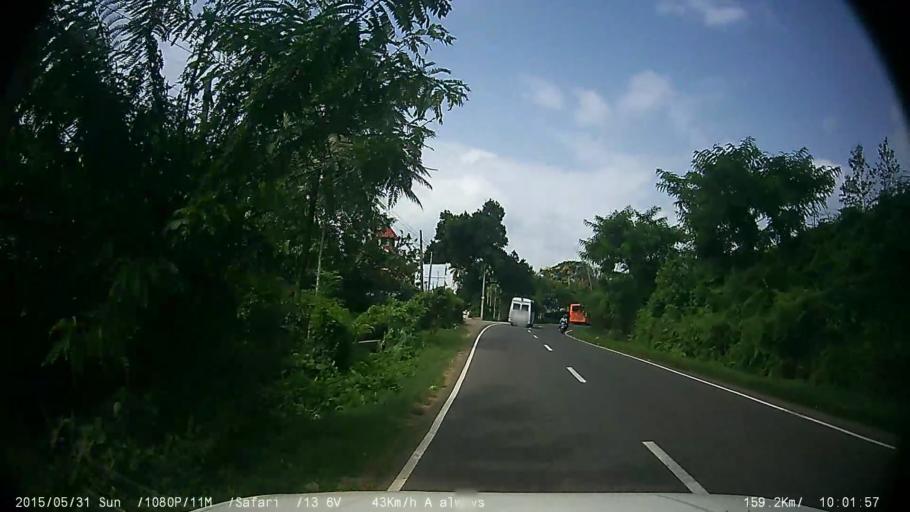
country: IN
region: Kerala
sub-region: Wayanad
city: Kalpetta
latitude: 11.5773
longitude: 76.0604
